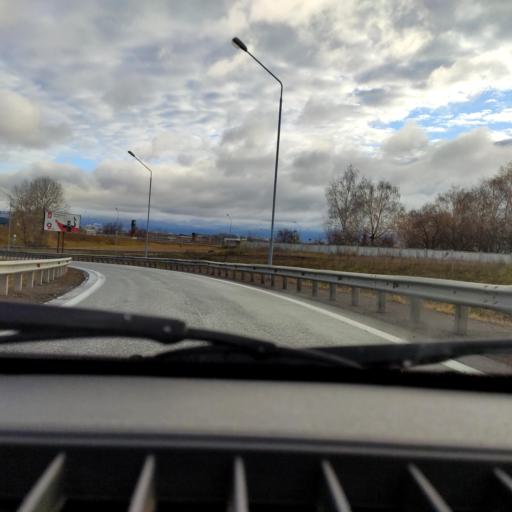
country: RU
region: Bashkortostan
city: Avdon
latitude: 54.6746
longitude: 55.8010
